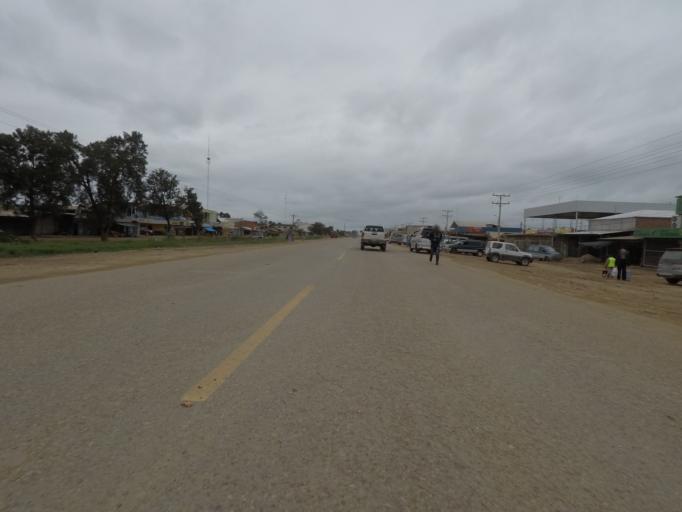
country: BO
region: Santa Cruz
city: Okinawa Numero Uno
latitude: -17.2644
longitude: -62.5553
